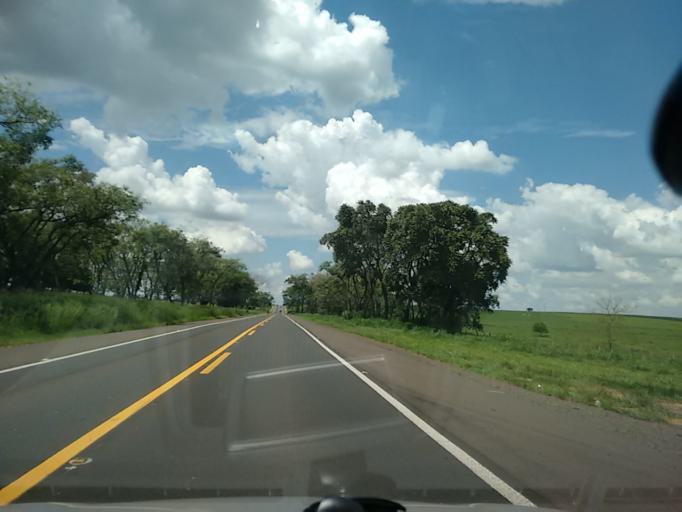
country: BR
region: Sao Paulo
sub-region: Osvaldo Cruz
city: Osvaldo Cruz
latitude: -21.8766
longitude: -50.8604
